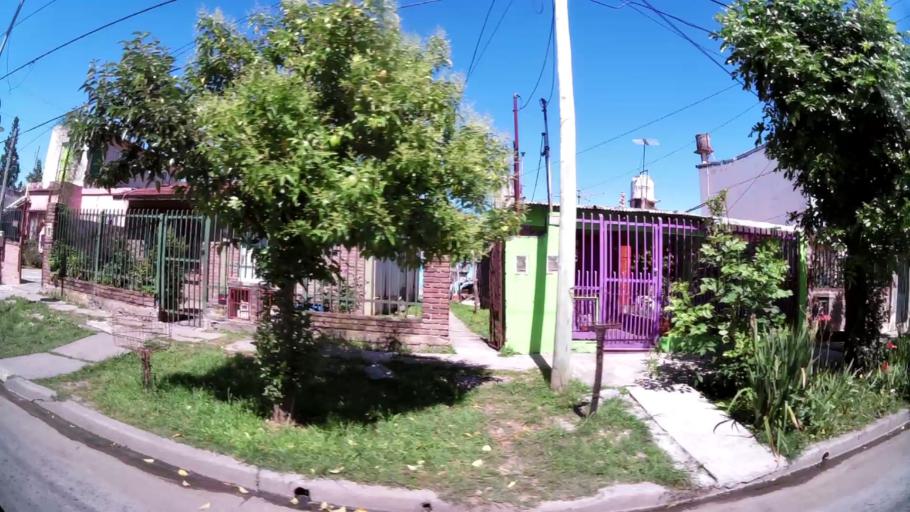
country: AR
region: Buenos Aires
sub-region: Partido de Tigre
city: Tigre
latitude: -34.5037
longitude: -58.6102
